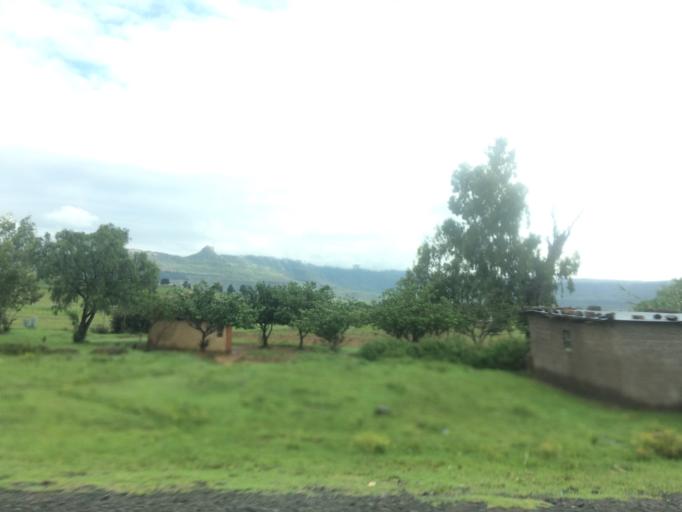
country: LS
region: Mafeteng
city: Mafeteng
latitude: -29.7129
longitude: 27.4819
